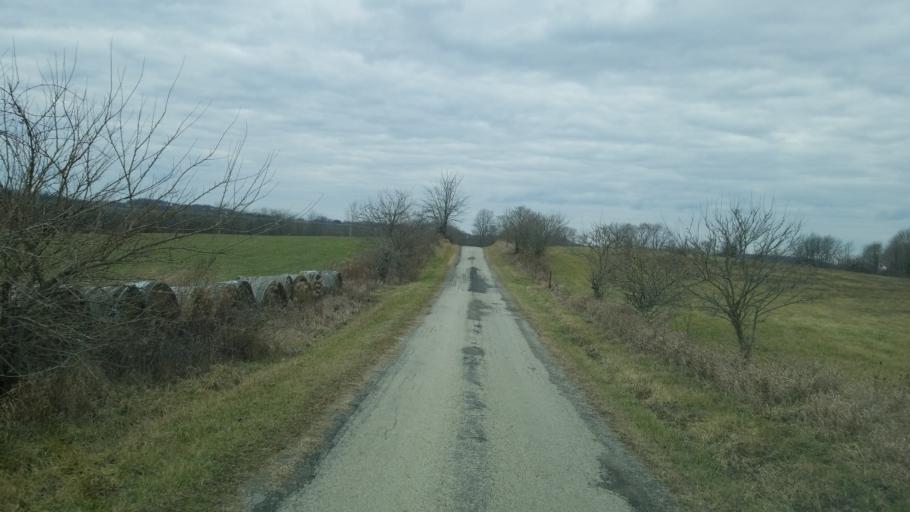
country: US
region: Ohio
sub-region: Highland County
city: Greenfield
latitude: 39.3197
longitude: -83.3426
